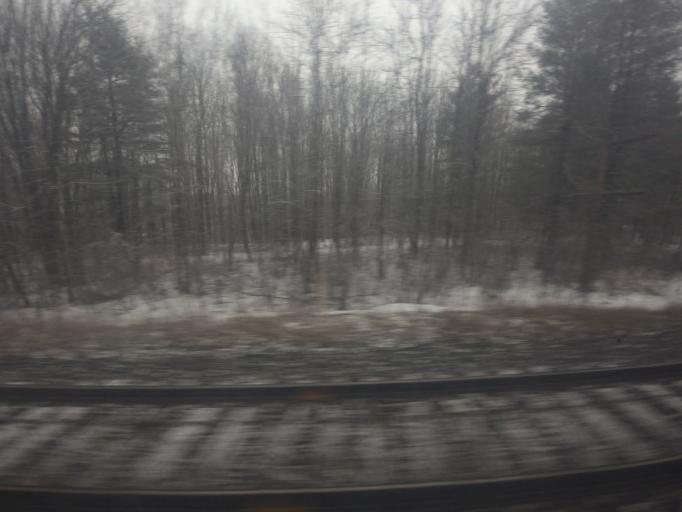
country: CA
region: Ontario
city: Brockville
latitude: 44.5653
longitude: -75.7768
